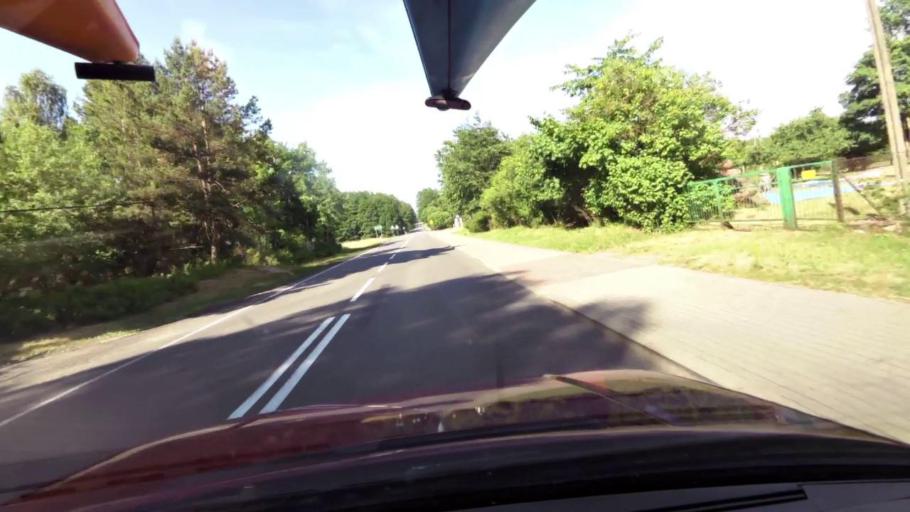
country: PL
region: Pomeranian Voivodeship
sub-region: Powiat bytowski
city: Trzebielino
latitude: 54.1438
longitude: 17.0311
